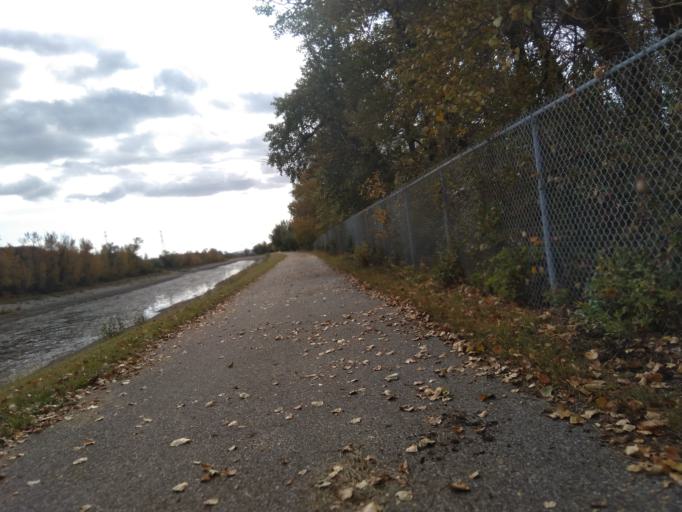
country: CA
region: Alberta
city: Calgary
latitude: 51.0221
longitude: -114.0051
